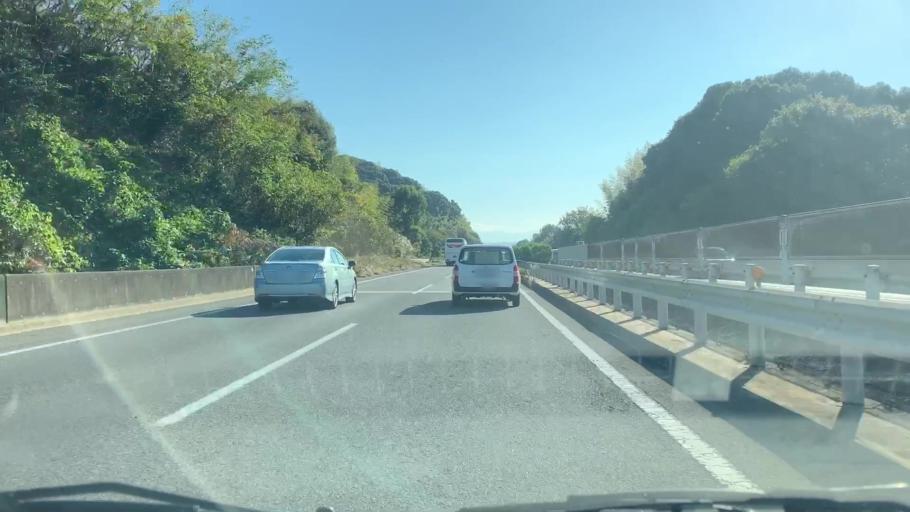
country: JP
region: Saga Prefecture
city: Saga-shi
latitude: 33.3097
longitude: 130.2210
